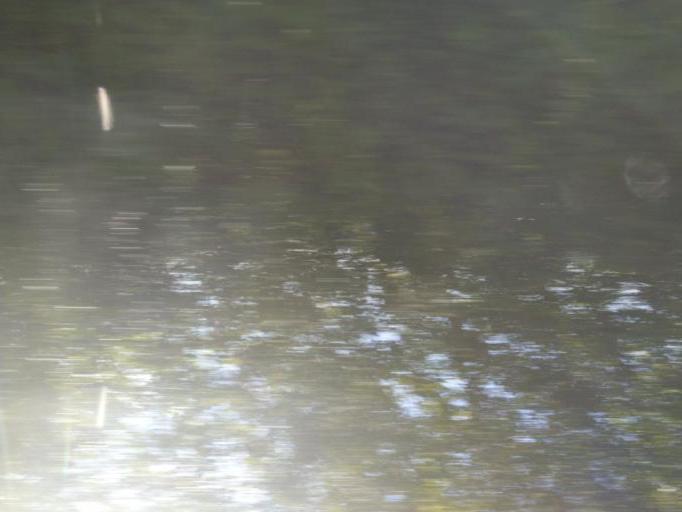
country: DE
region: Baden-Wuerttemberg
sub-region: Freiburg Region
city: Dogern
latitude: 47.6159
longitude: 8.1802
